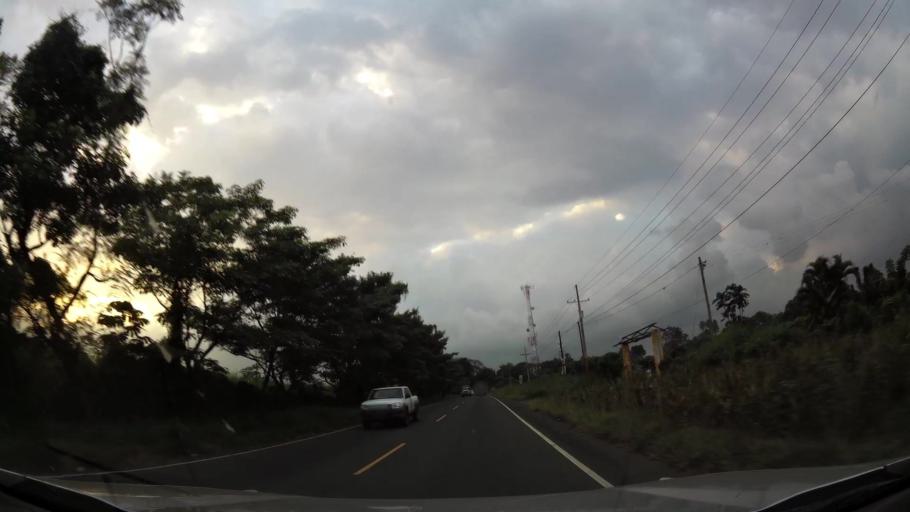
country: GT
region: Escuintla
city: Siquinala
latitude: 14.3009
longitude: -90.9547
